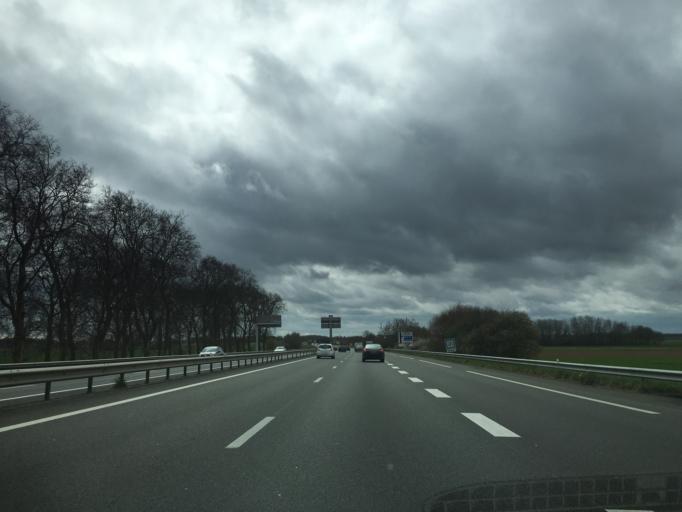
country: FR
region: Ile-de-France
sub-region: Departement de Seine-et-Marne
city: Moissy-Cramayel
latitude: 48.6296
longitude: 2.6288
